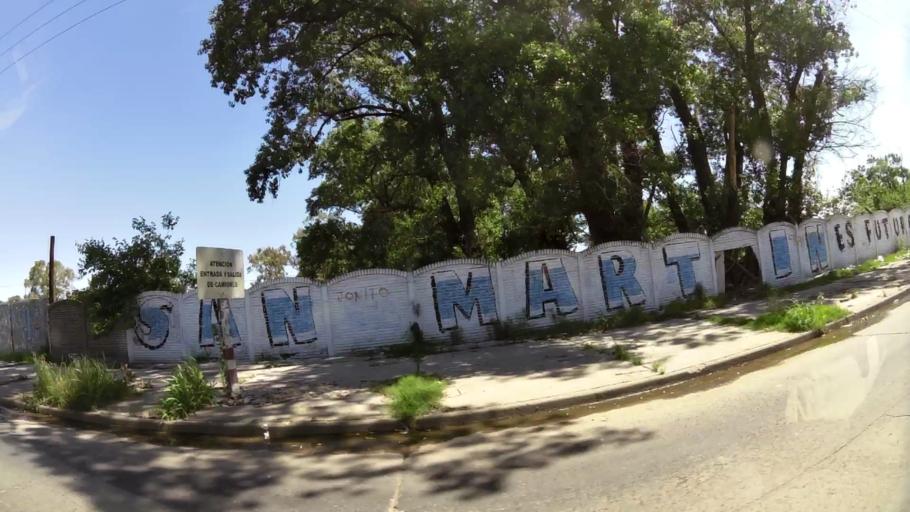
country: AR
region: Buenos Aires
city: Caseros
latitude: -34.5629
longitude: -58.5820
